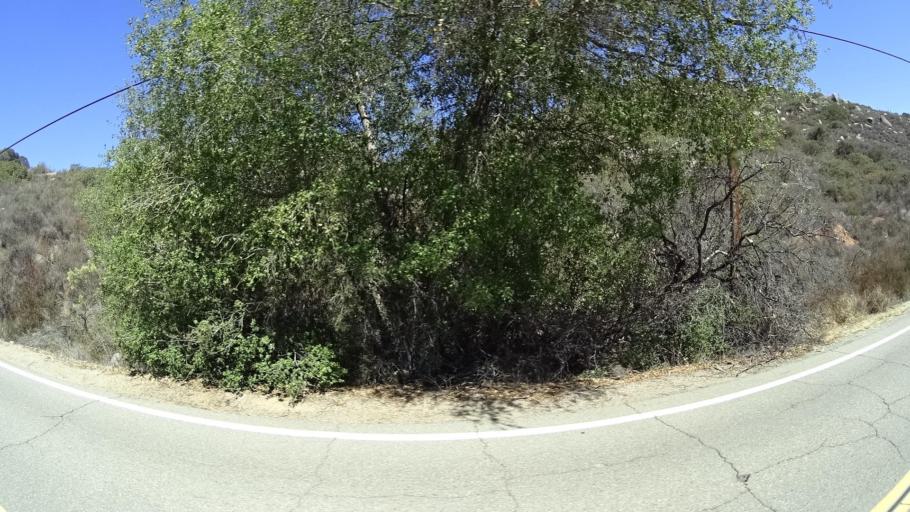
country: US
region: California
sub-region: San Diego County
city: Alpine
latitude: 32.8024
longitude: -116.7651
